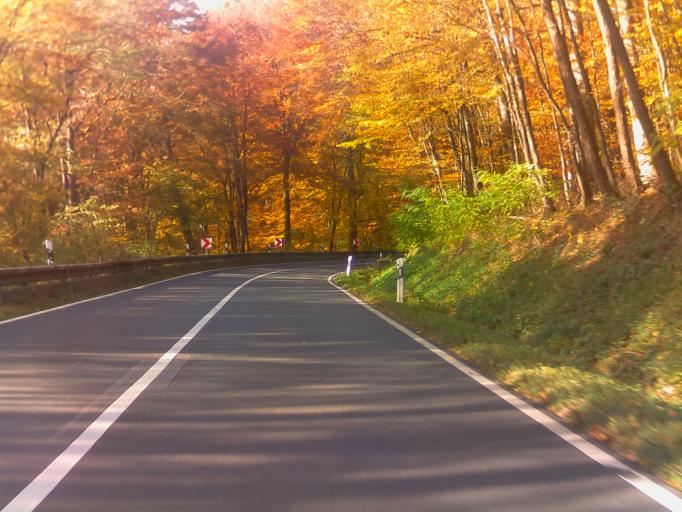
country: DE
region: Bavaria
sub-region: Regierungsbezirk Unterfranken
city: Oberschwarzach
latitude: 49.8482
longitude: 10.4645
